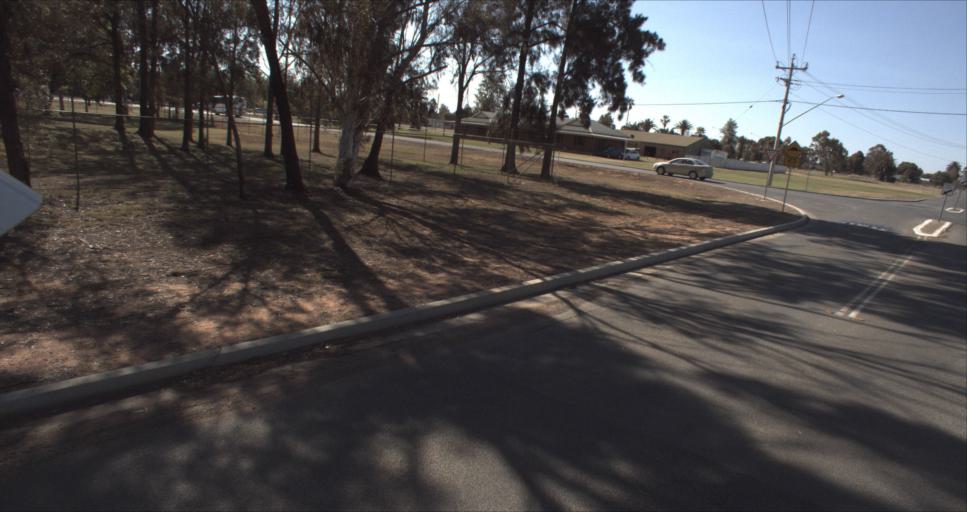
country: AU
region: New South Wales
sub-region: Leeton
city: Leeton
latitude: -34.5639
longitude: 146.4148
